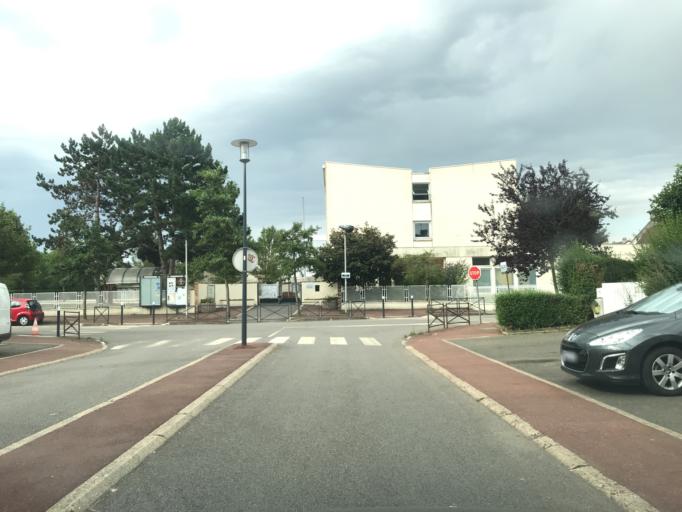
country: FR
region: Ile-de-France
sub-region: Departement des Yvelines
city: Maurepas
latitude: 48.7642
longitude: 1.9358
